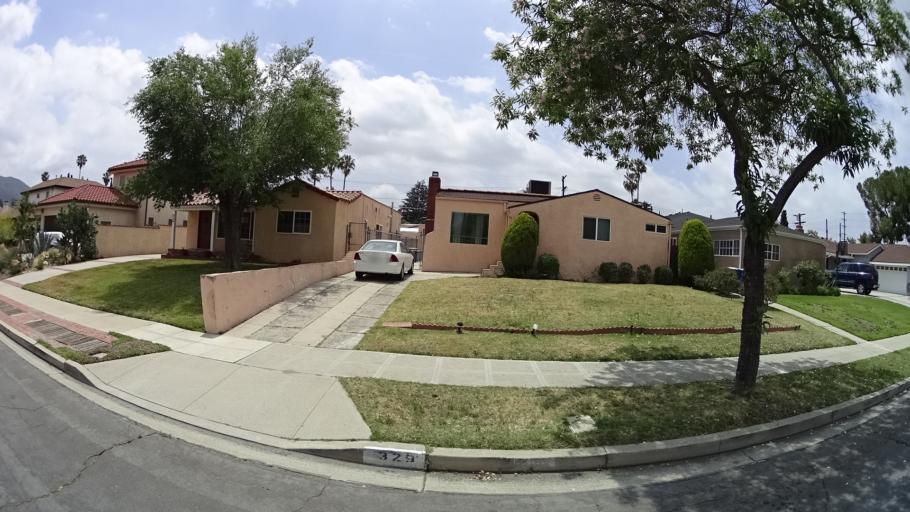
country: US
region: California
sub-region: Los Angeles County
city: Burbank
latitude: 34.1635
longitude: -118.3332
